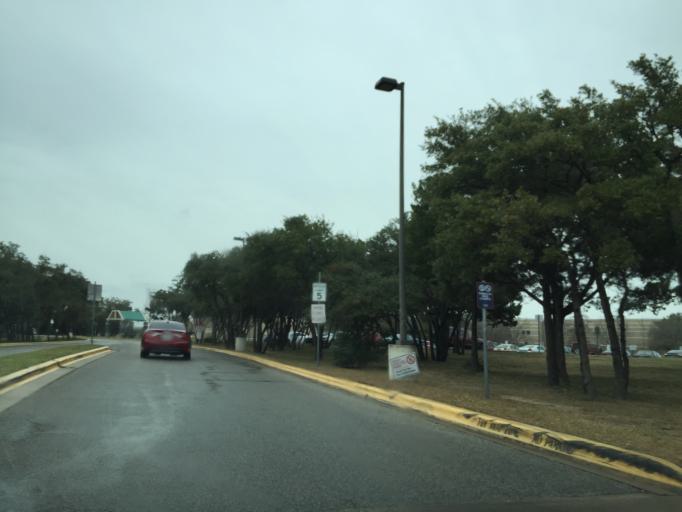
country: US
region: Texas
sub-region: Travis County
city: Wells Branch
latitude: 30.4017
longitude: -97.7052
